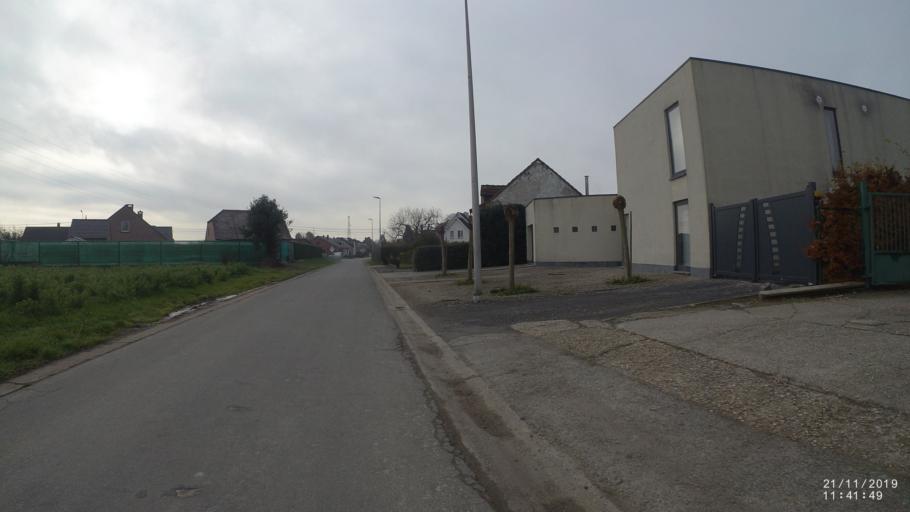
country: BE
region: Flanders
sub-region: Provincie Limburg
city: Sint-Truiden
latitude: 50.8212
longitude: 5.2243
